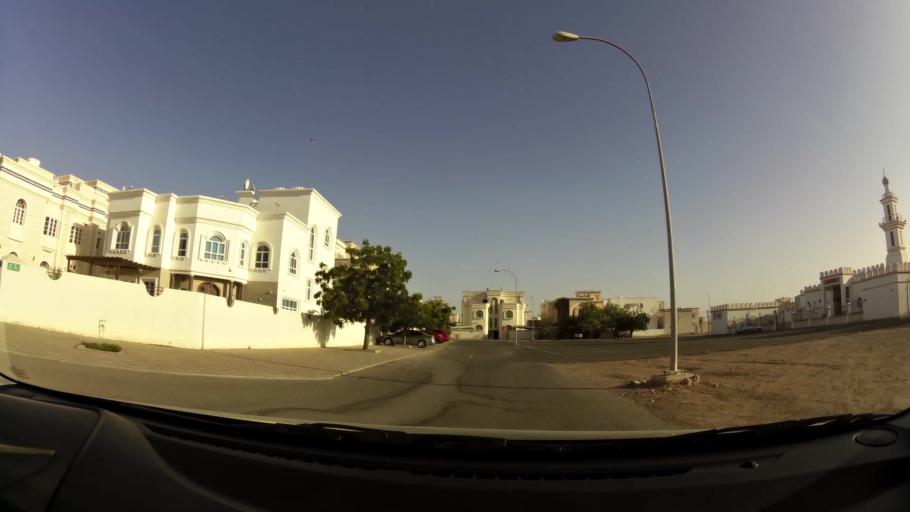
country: OM
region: Muhafazat Masqat
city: As Sib al Jadidah
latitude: 23.6132
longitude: 58.2186
